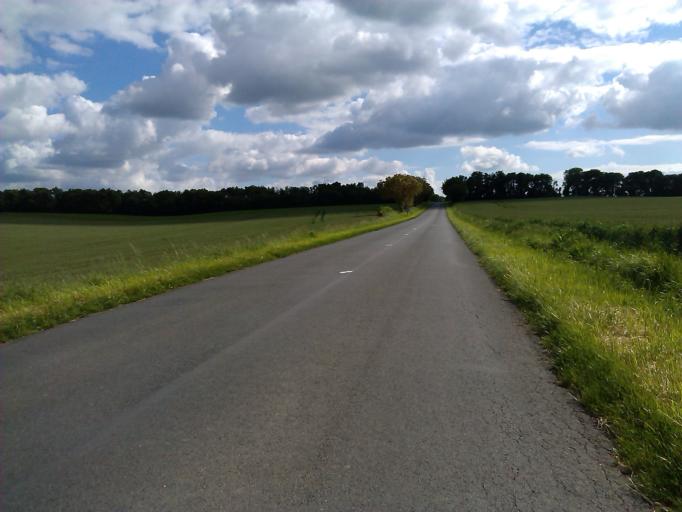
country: FR
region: Poitou-Charentes
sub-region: Departement de la Charente
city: Mansle
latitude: 45.8576
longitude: 0.1652
